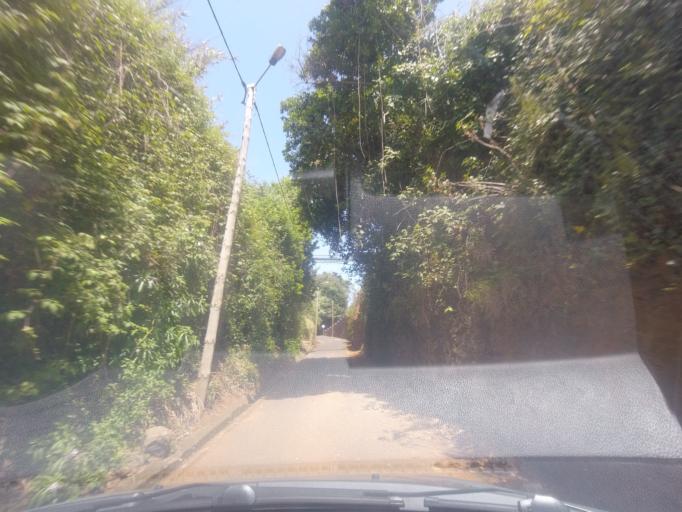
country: PT
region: Madeira
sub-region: Calheta
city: Faja da Ovelha
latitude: 32.8005
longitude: -17.2379
